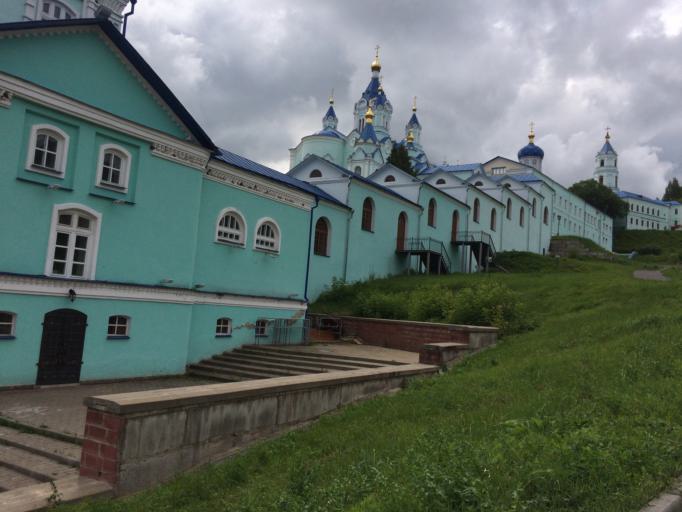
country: RU
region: Kursk
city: Zolotukhino
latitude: 51.9721
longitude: 36.3164
